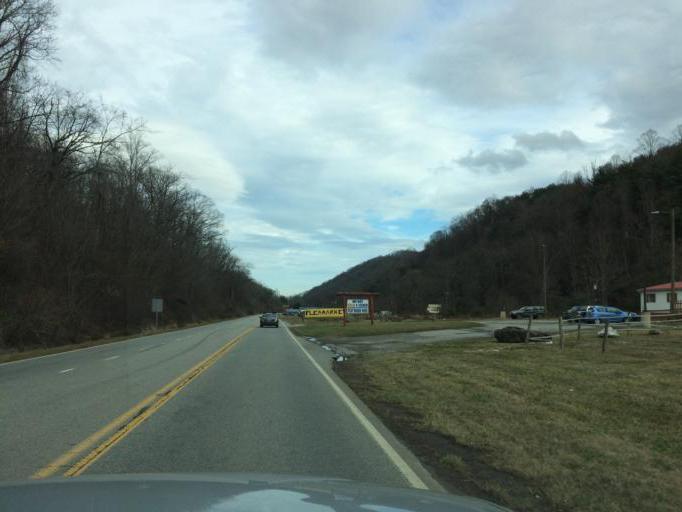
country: US
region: North Carolina
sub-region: Haywood County
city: Canton
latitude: 35.5361
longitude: -82.8052
